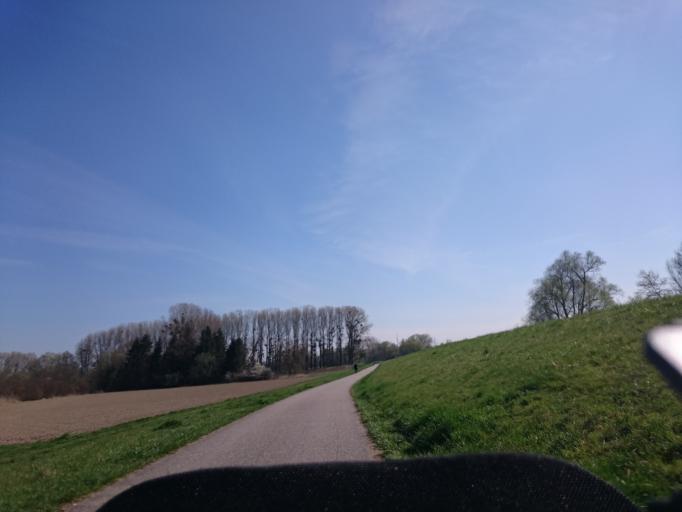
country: DE
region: Rheinland-Pfalz
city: Worth am Rhein
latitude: 49.0262
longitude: 8.2909
